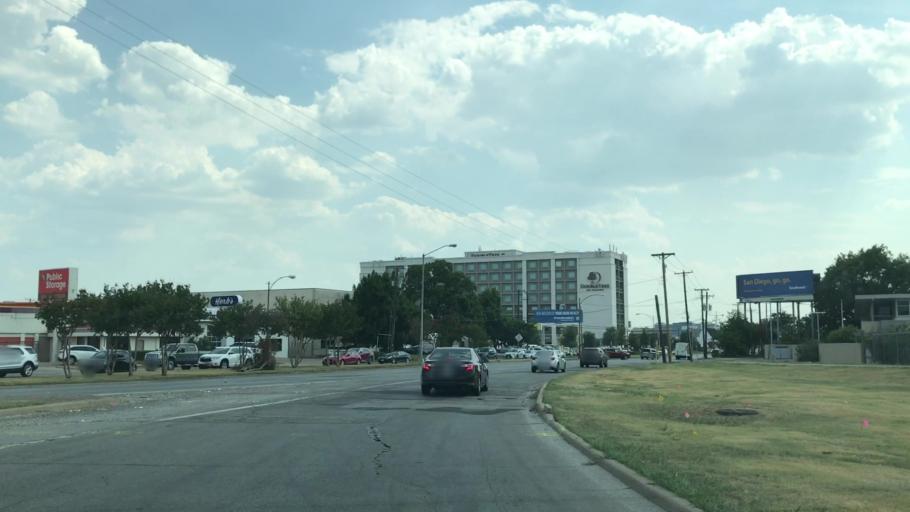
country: US
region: Texas
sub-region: Dallas County
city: University Park
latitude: 32.8365
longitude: -96.8348
